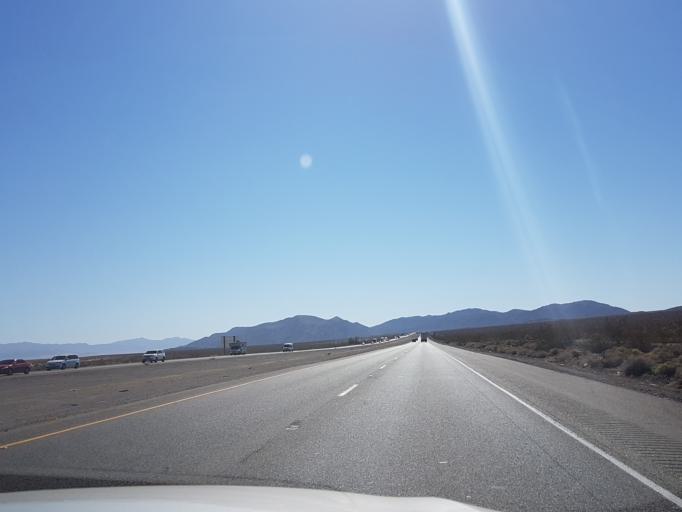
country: US
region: California
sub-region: San Bernardino County
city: Fort Irwin
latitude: 35.2450
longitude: -116.0948
